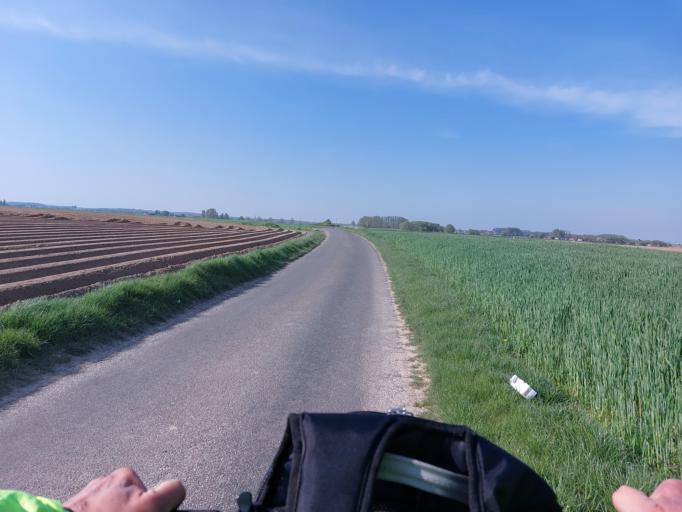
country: BE
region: Wallonia
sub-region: Province du Hainaut
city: Ecaussinnes-d'Enghien
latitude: 50.5518
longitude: 4.1525
